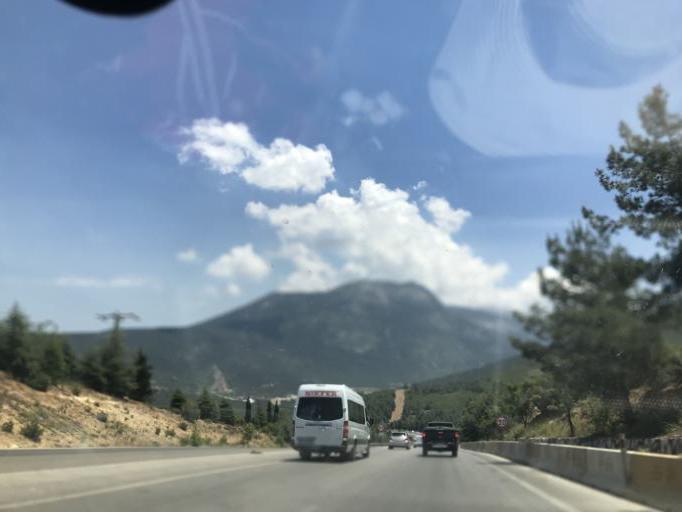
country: TR
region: Denizli
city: Honaz
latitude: 37.7324
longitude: 29.1809
